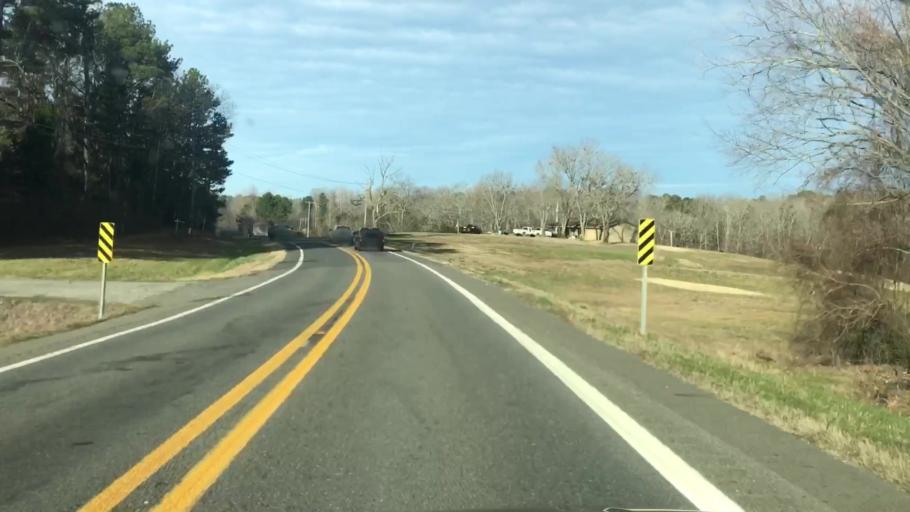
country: US
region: Arkansas
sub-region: Montgomery County
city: Mount Ida
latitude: 34.5315
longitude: -93.5327
